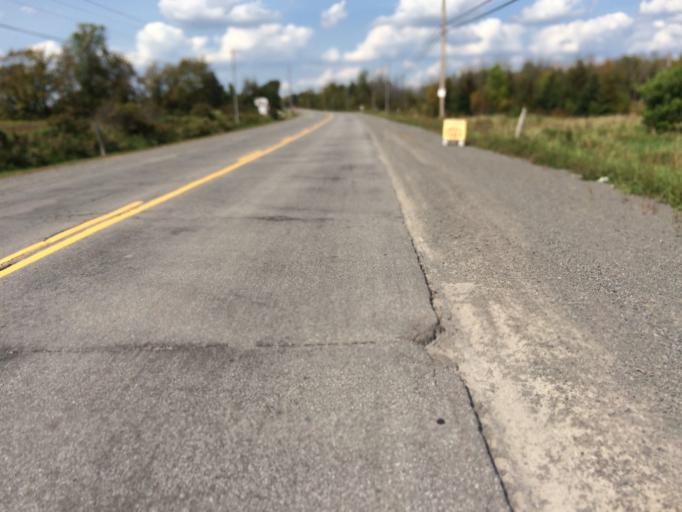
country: CA
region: Ontario
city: Ottawa
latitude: 45.1939
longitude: -75.6411
